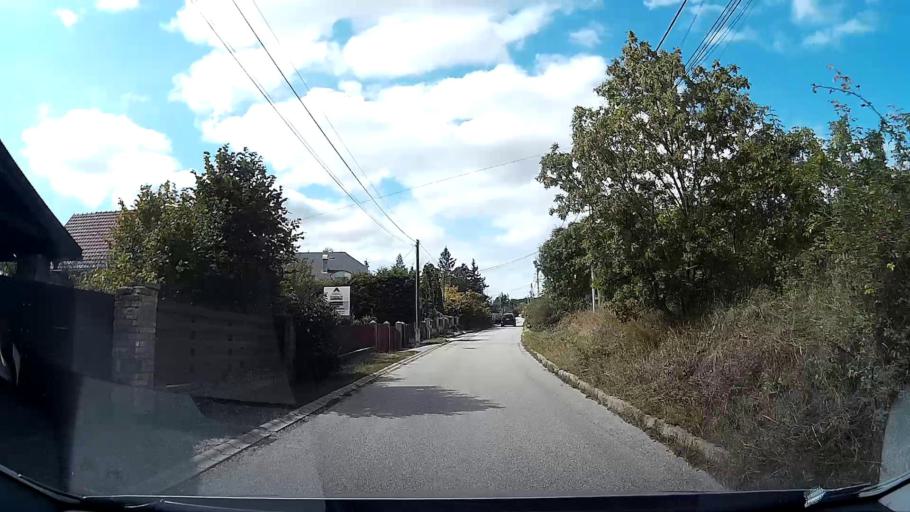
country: HU
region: Pest
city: Szentendre
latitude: 47.6910
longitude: 19.0707
